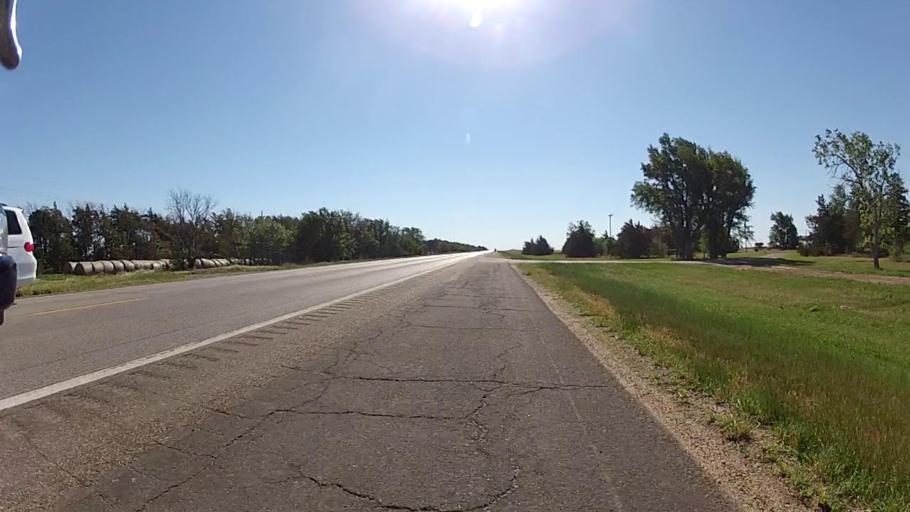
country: US
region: Kansas
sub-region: Kiowa County
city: Greensburg
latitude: 37.5864
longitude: -99.5851
